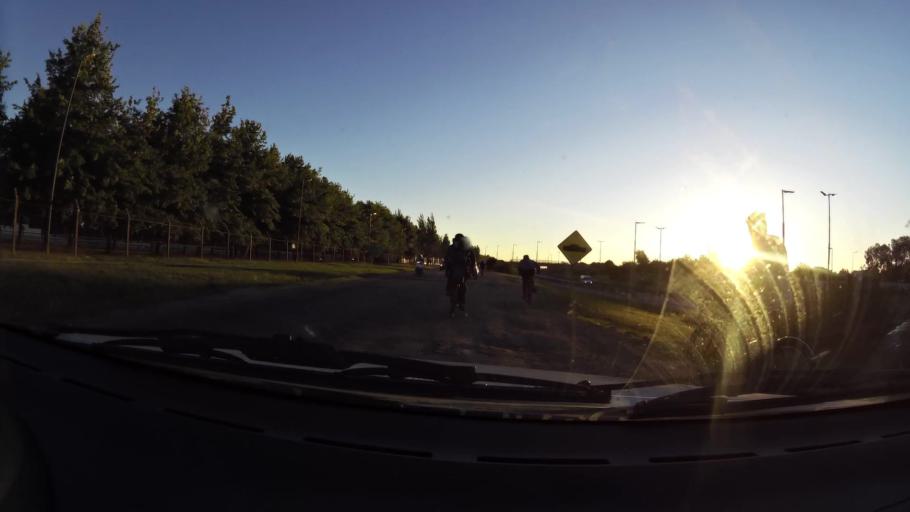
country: AR
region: Buenos Aires
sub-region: Partido de Quilmes
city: Quilmes
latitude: -34.7999
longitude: -58.1627
